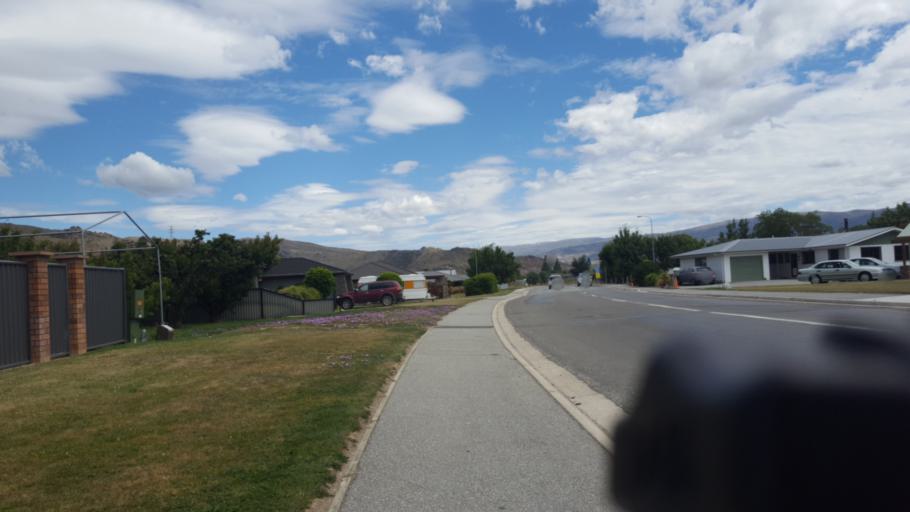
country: NZ
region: Otago
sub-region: Queenstown-Lakes District
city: Wanaka
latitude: -45.0391
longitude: 169.2158
